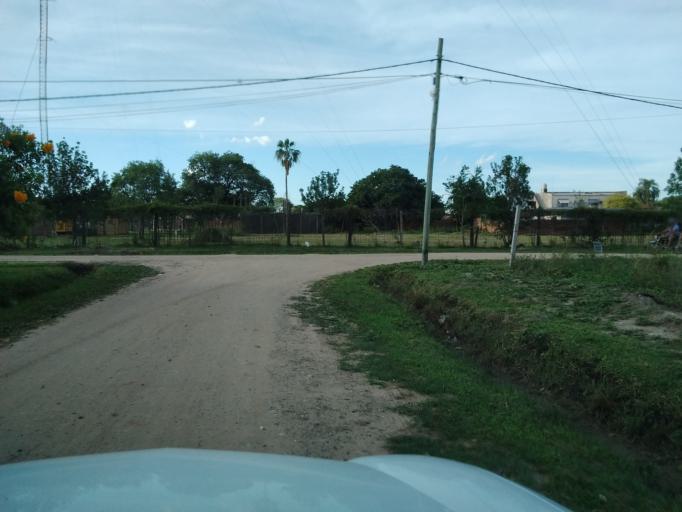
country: AR
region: Corrientes
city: Corrientes
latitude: -27.4905
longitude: -58.8472
